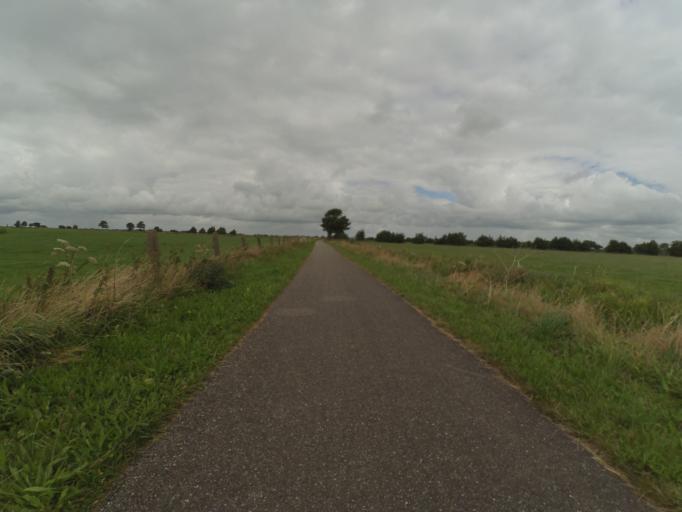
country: NL
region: Friesland
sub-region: Gemeente Kollumerland en Nieuwkruisland
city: Kollumerzwaag
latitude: 53.2898
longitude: 6.1087
